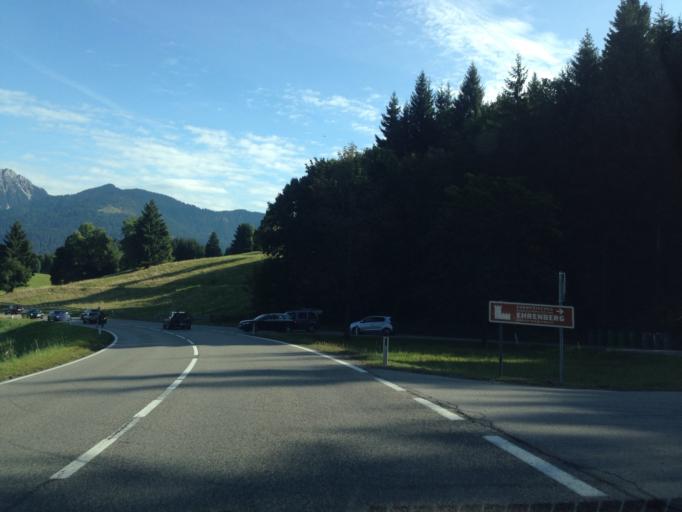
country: AT
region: Tyrol
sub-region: Politischer Bezirk Reutte
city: Breitenwang
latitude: 47.4677
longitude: 10.7250
